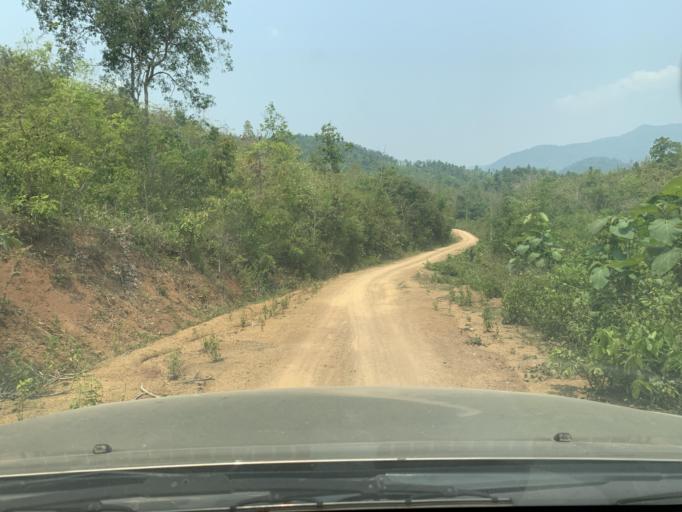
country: LA
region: Louangphabang
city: Louangphabang
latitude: 19.9511
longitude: 102.1295
